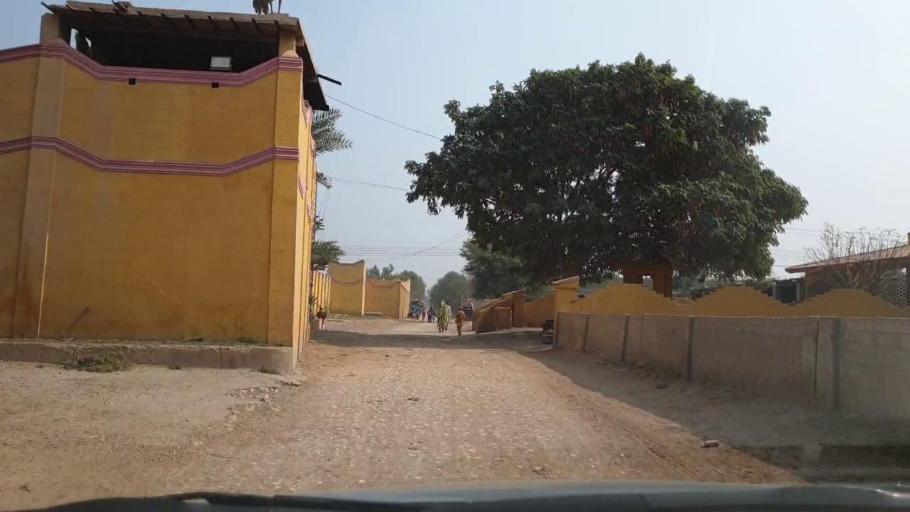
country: PK
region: Sindh
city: Matiari
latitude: 25.6580
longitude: 68.5395
